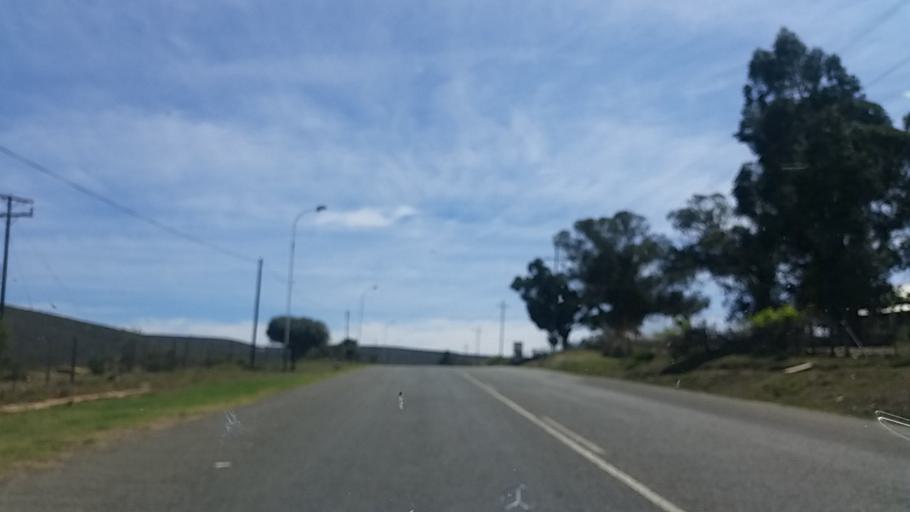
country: ZA
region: Western Cape
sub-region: Eden District Municipality
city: Knysna
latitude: -33.6529
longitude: 23.1348
